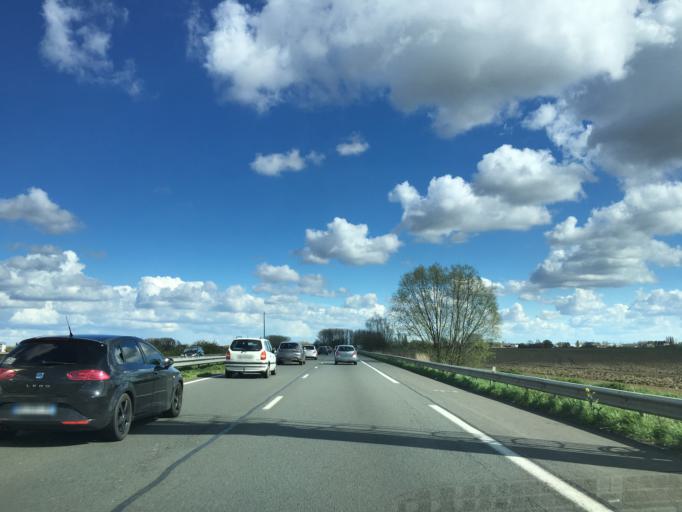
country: FR
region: Nord-Pas-de-Calais
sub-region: Departement du Nord
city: Armentieres
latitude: 50.6713
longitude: 2.8714
